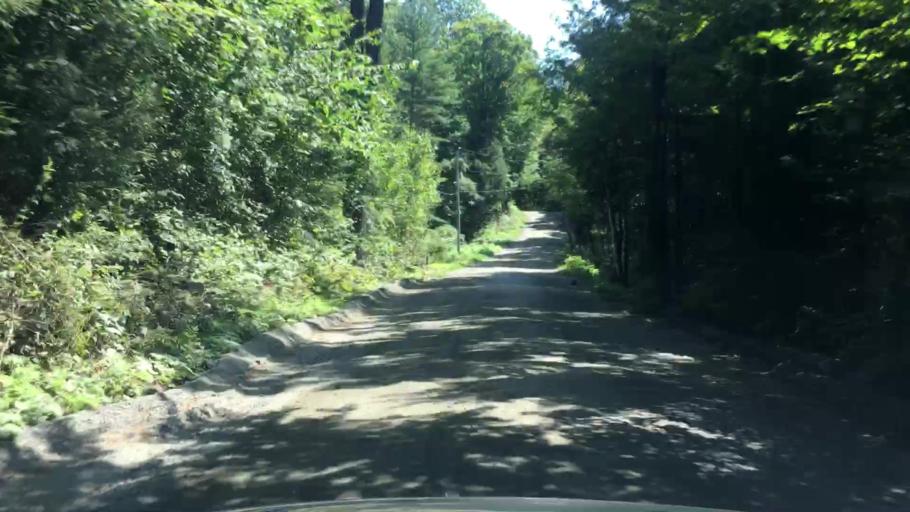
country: US
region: Vermont
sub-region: Windham County
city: West Brattleboro
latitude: 42.7986
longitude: -72.6393
